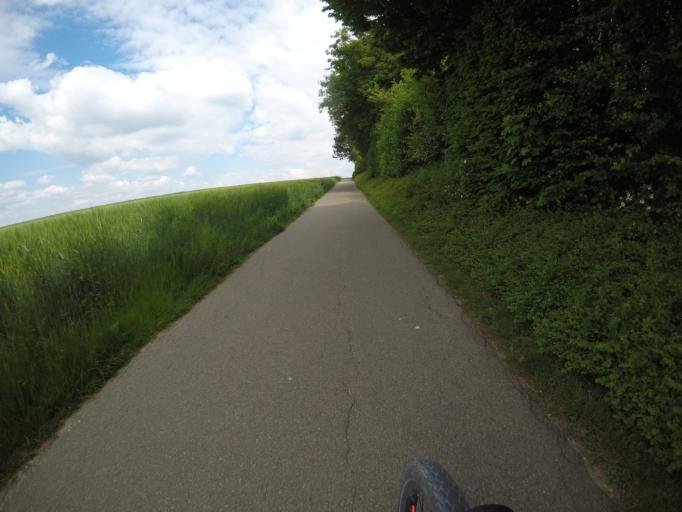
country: DE
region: Baden-Wuerttemberg
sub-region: Regierungsbezirk Stuttgart
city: Kongen
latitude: 48.6922
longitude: 9.3669
